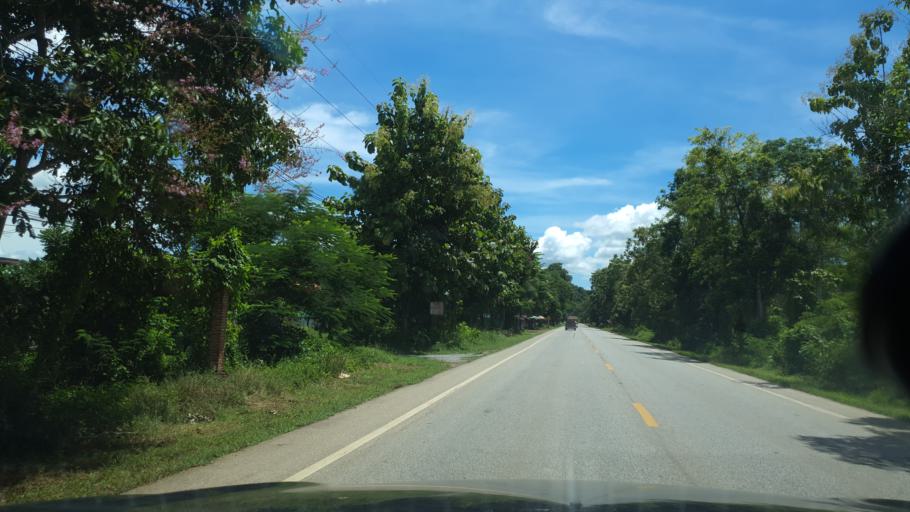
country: TH
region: Sukhothai
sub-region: Amphoe Si Satchanalai
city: Si Satchanalai
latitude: 17.4459
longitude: 99.7923
